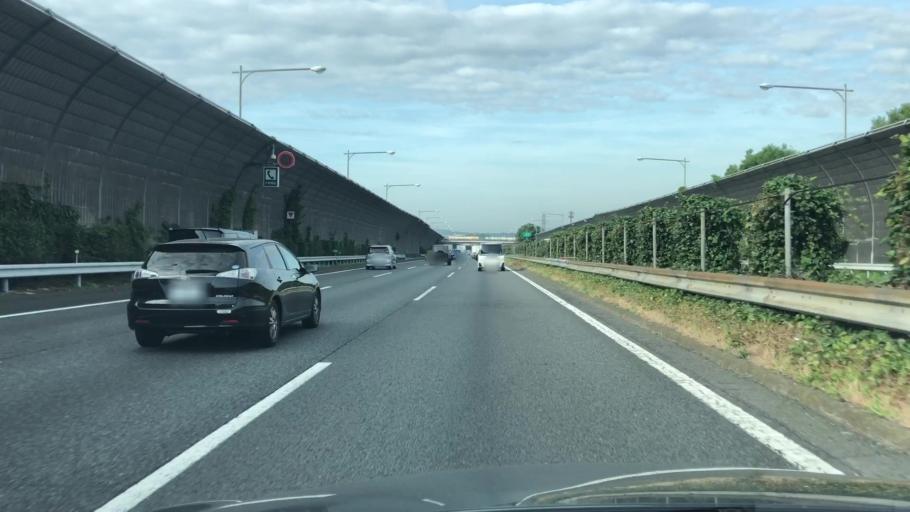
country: JP
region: Kanagawa
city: Isehara
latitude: 35.3979
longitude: 139.2861
